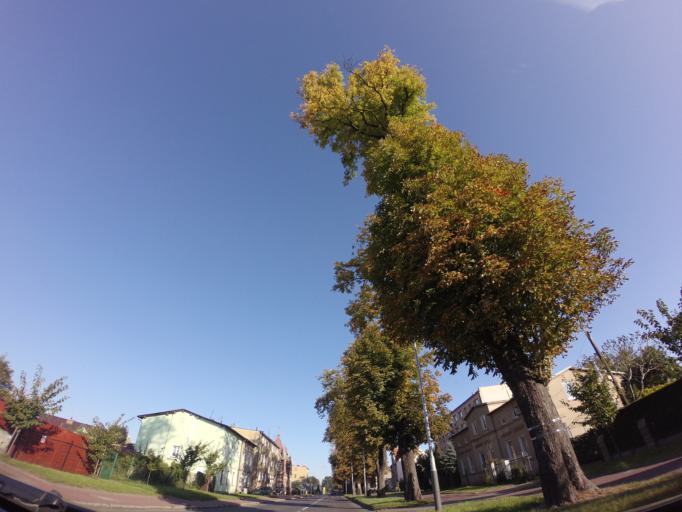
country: PL
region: West Pomeranian Voivodeship
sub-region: Powiat goleniowski
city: Maszewo
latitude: 53.4995
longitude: 15.0577
